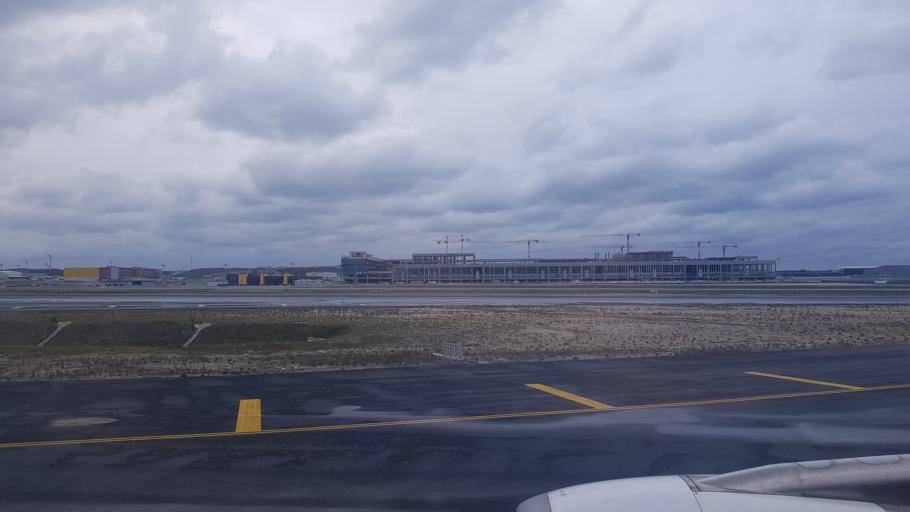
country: TR
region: Istanbul
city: Durusu
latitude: 41.2762
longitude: 28.7296
